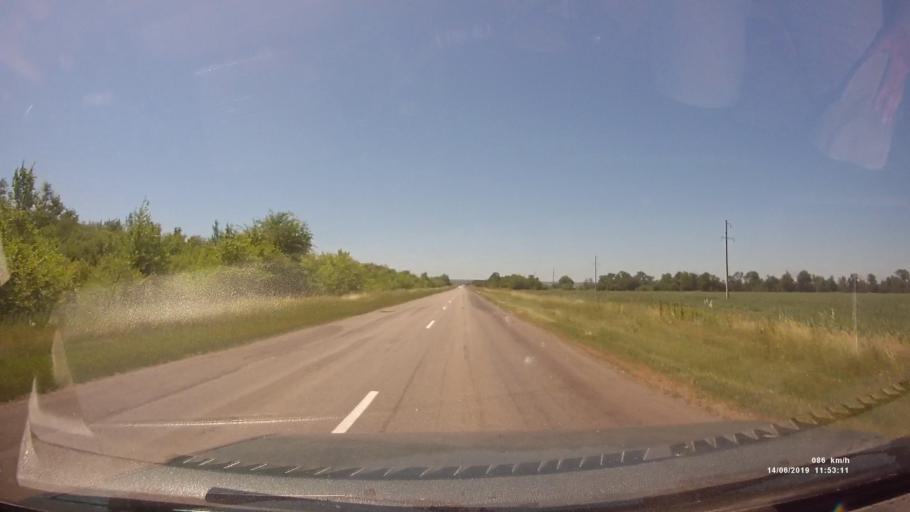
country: RU
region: Rostov
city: Kazanskaya
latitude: 49.8298
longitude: 41.2163
